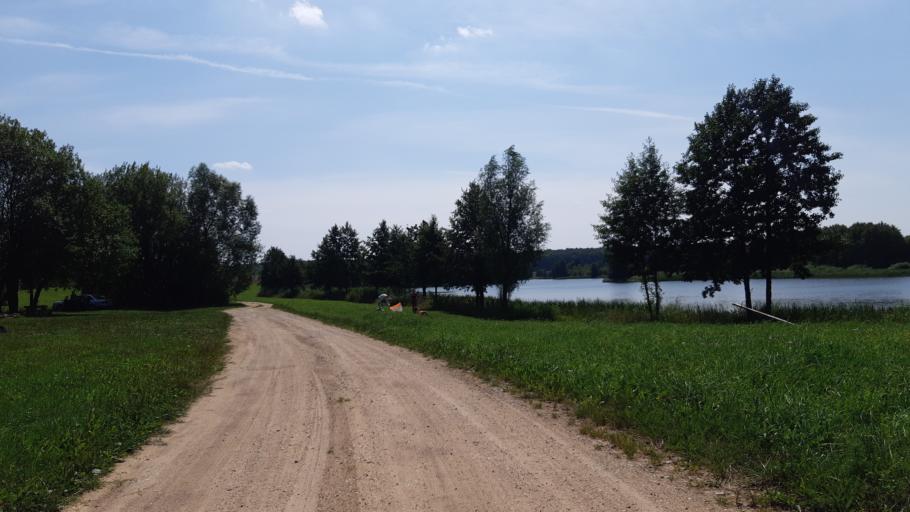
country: LT
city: Virbalis
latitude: 54.6186
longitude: 22.8036
